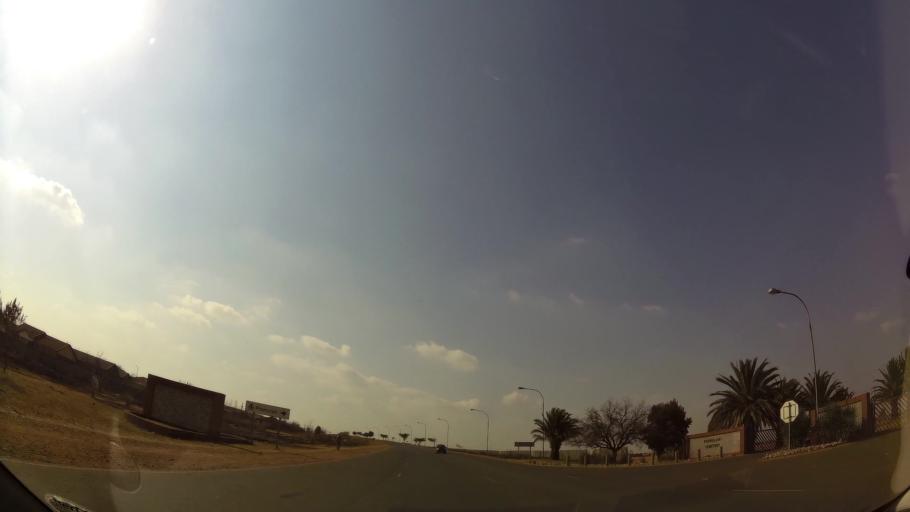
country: ZA
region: Gauteng
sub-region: Ekurhuleni Metropolitan Municipality
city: Springs
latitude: -26.1356
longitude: 28.4686
